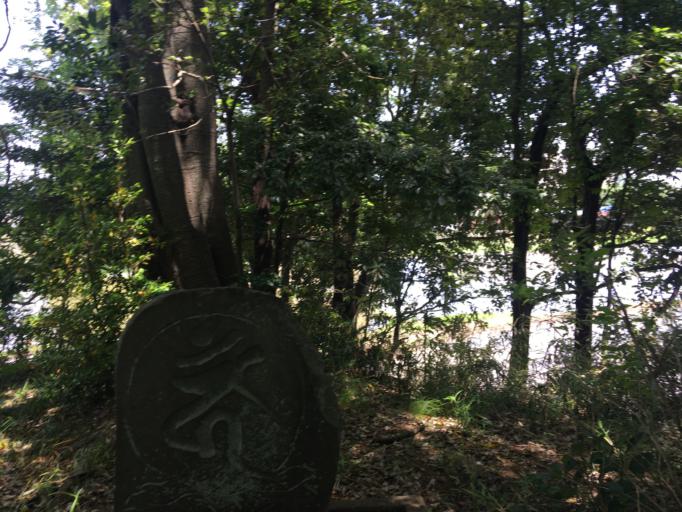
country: JP
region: Saitama
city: Kasukabe
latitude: 35.9764
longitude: 139.7119
